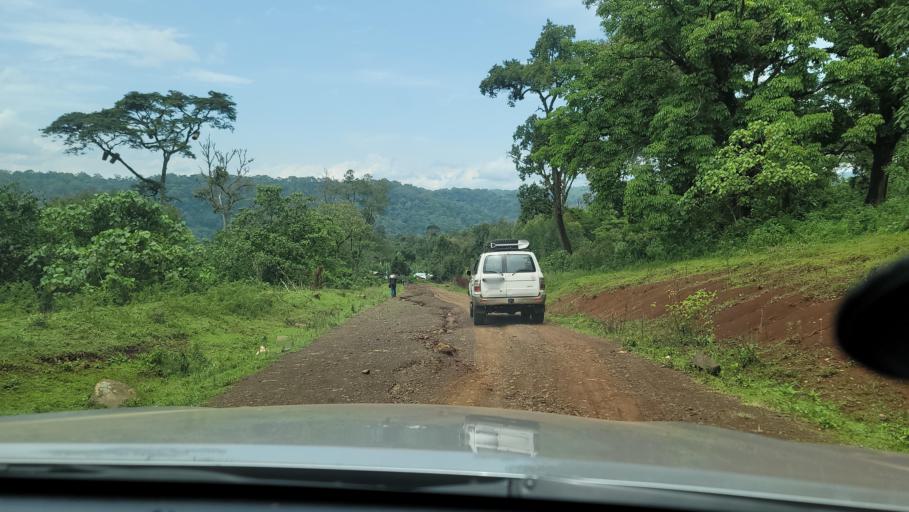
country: ET
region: Oromiya
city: Agaro
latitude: 7.7057
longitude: 36.2532
